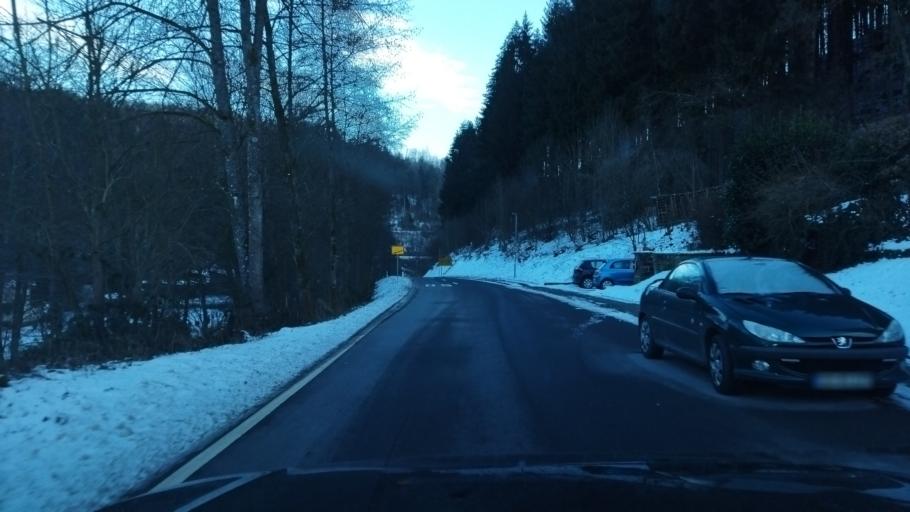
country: DE
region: Baden-Wuerttemberg
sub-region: Karlsruhe Region
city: Eberbach
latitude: 49.4960
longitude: 9.0426
